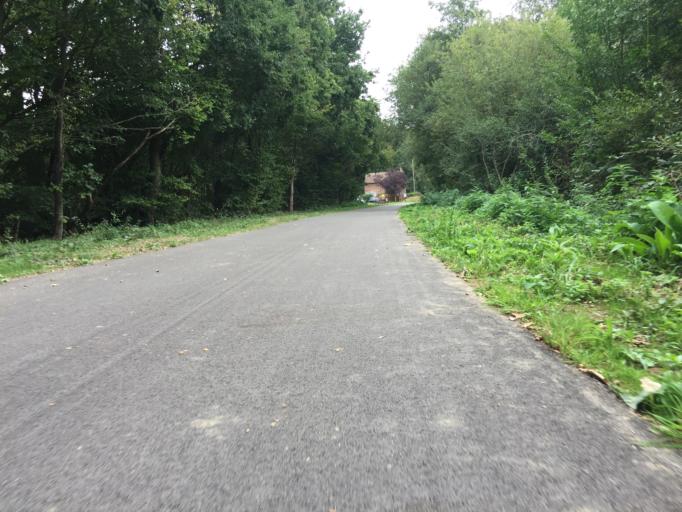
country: FR
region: Picardie
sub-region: Departement de l'Oise
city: Saint-Paul
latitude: 49.4131
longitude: 2.0167
